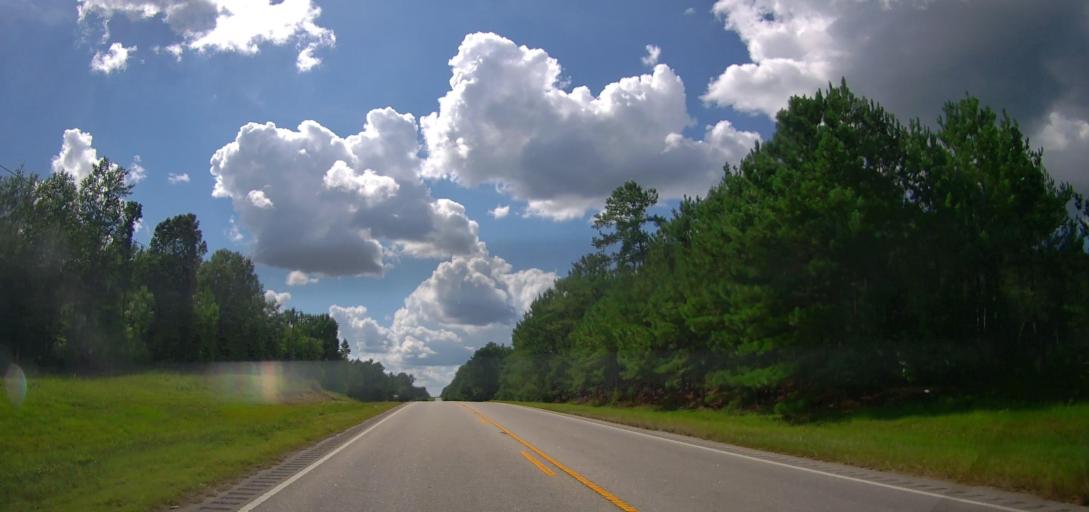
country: US
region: Alabama
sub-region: Macon County
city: Tuskegee
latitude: 32.4550
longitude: -85.5388
